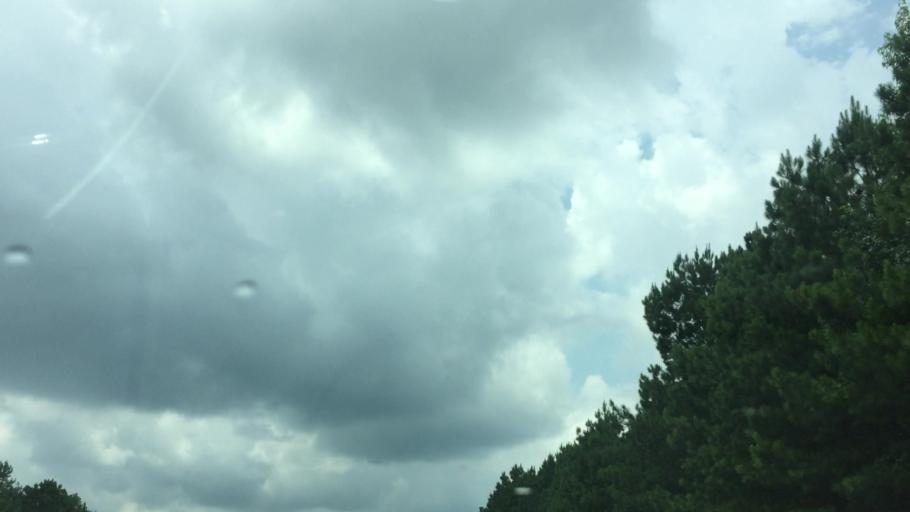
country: US
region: Georgia
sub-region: Fulton County
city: Fairburn
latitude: 33.6099
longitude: -84.6157
